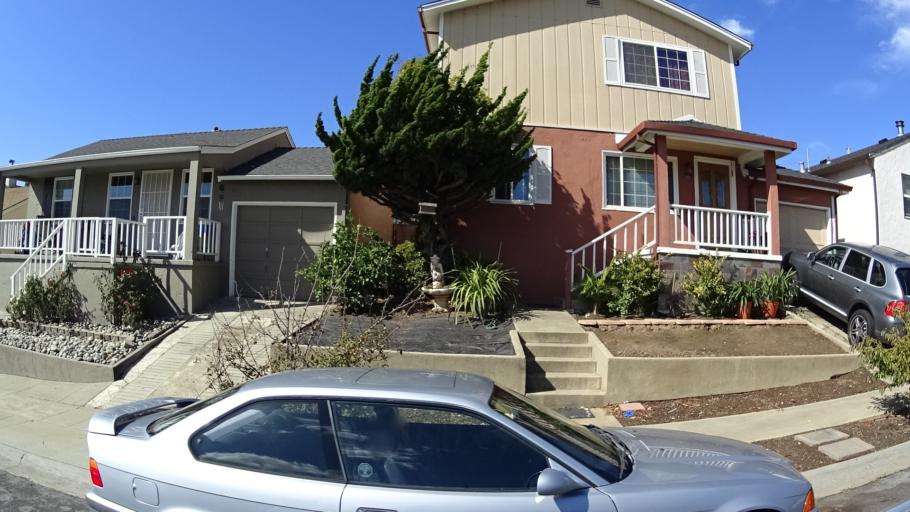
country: US
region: California
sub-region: San Mateo County
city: South San Francisco
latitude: 37.6655
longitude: -122.4091
